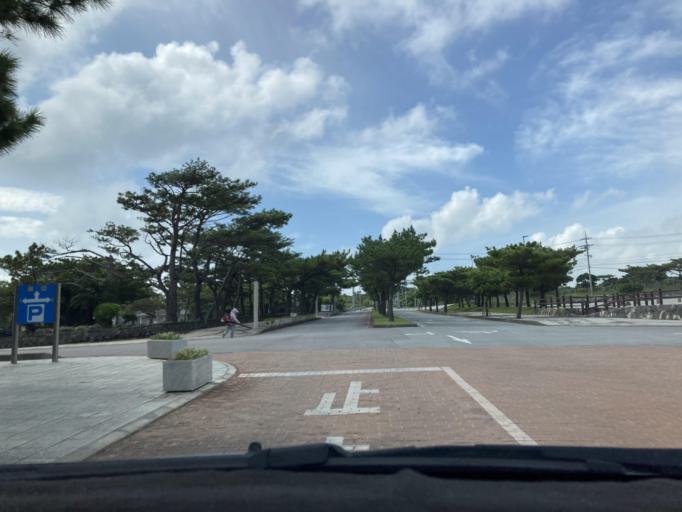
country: JP
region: Okinawa
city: Itoman
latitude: 26.0969
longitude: 127.7230
